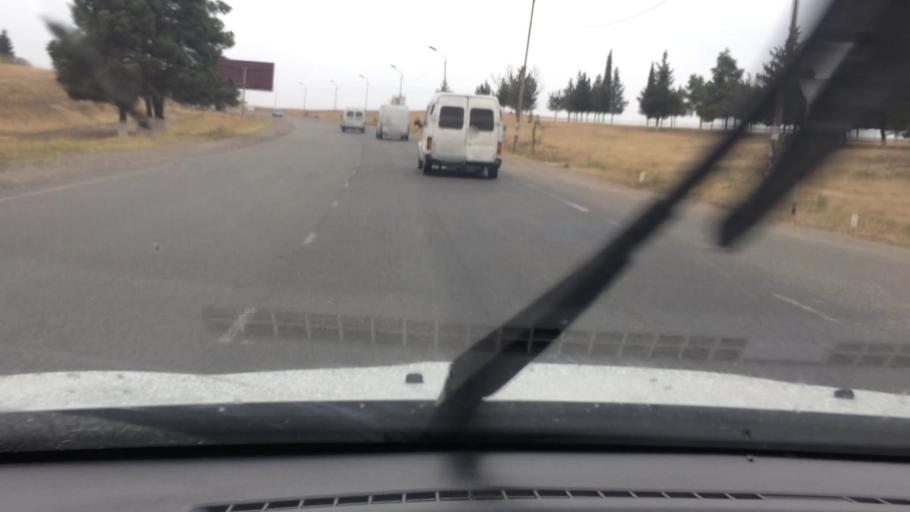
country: GE
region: Kvemo Kartli
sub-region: Marneuli
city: Marneuli
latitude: 41.5018
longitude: 44.8028
